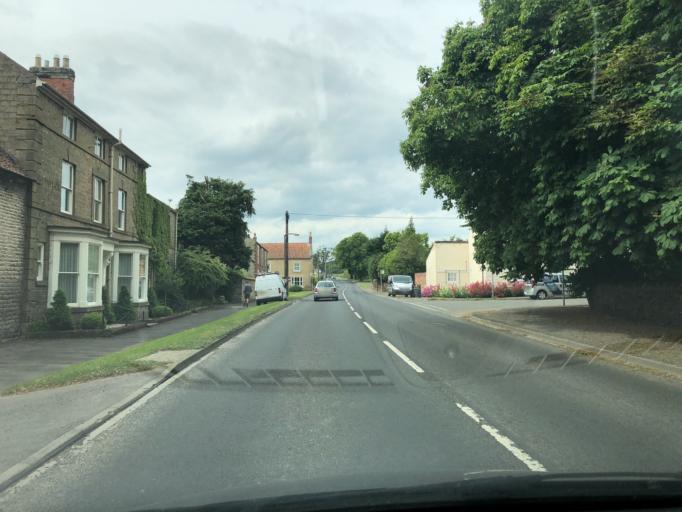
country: GB
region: England
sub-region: North Yorkshire
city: Pickering
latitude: 54.2579
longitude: -0.8015
